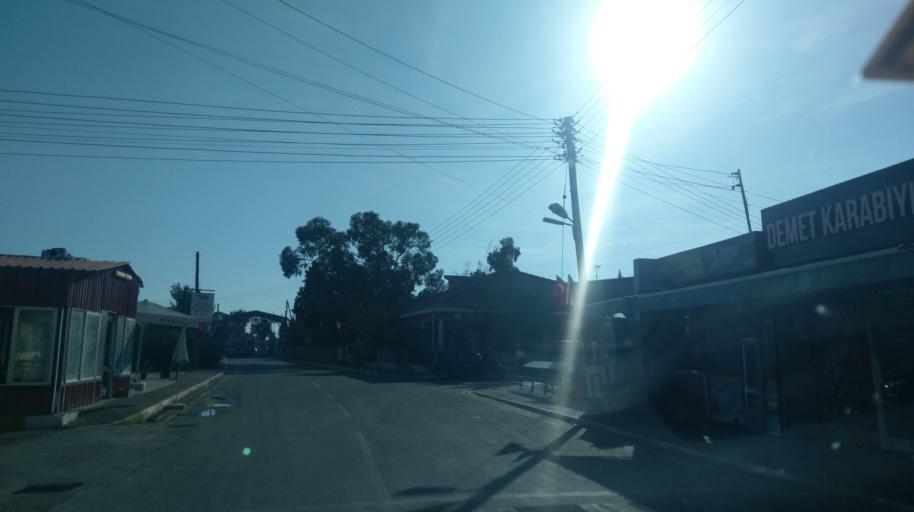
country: CY
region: Larnaka
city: Pergamos
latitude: 35.0396
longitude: 33.7072
